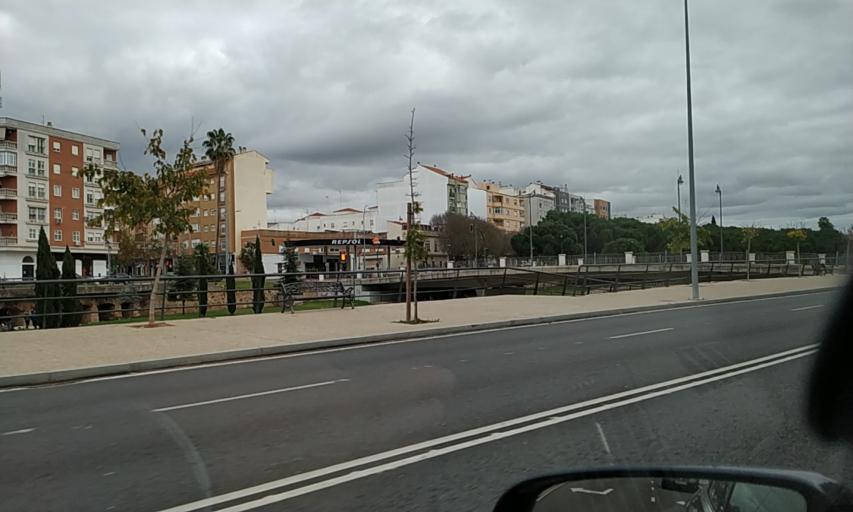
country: ES
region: Extremadura
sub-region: Provincia de Badajoz
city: Badajoz
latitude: 38.8791
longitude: -6.9635
